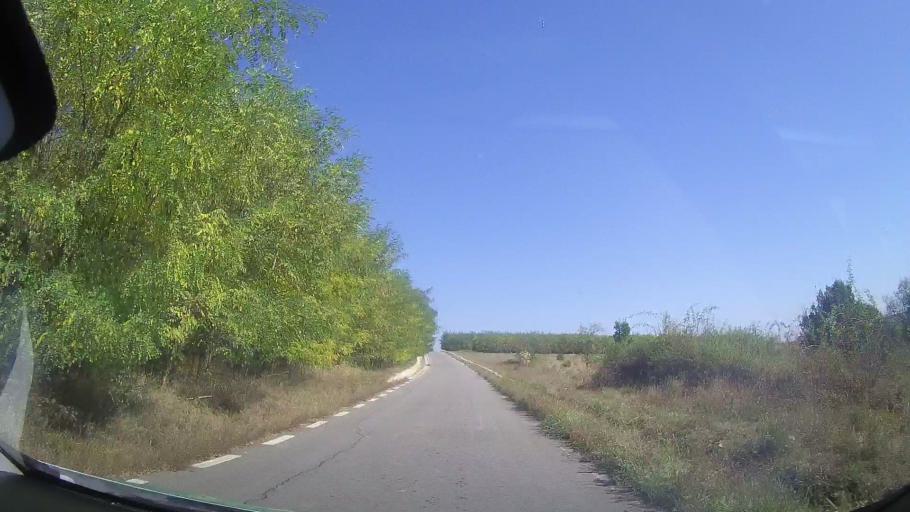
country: RO
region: Timis
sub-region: Comuna Ohaba Lunga
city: Ohaba Lunga
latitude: 45.9181
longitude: 21.9564
